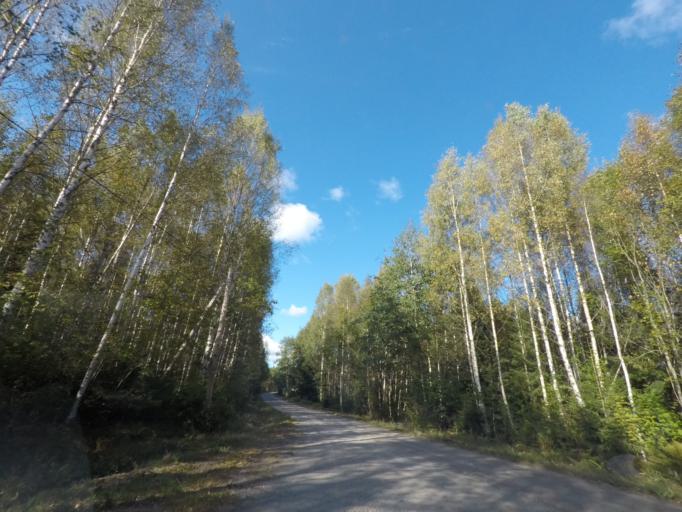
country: SE
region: Vaestmanland
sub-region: Skinnskattebergs Kommun
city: Skinnskatteberg
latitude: 59.8295
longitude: 15.5287
